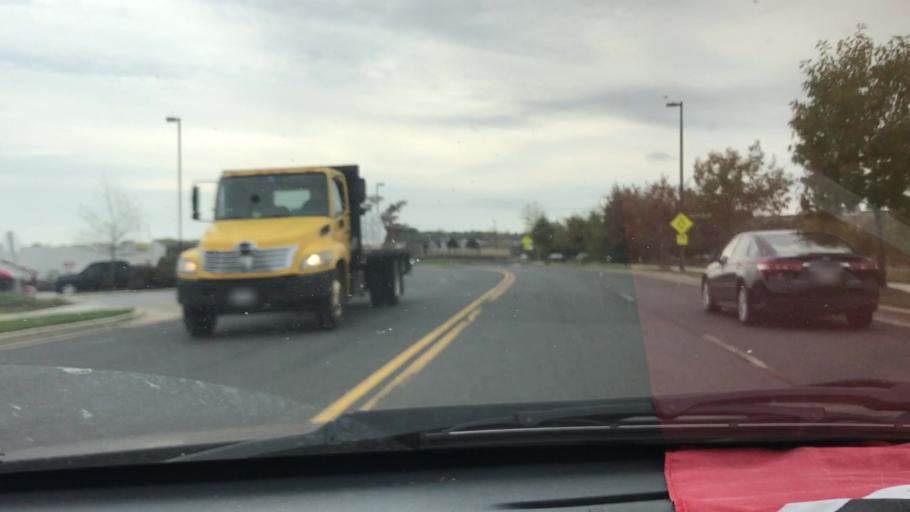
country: US
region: Maryland
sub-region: Prince George's County
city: Largo
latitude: 38.8728
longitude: -76.8507
